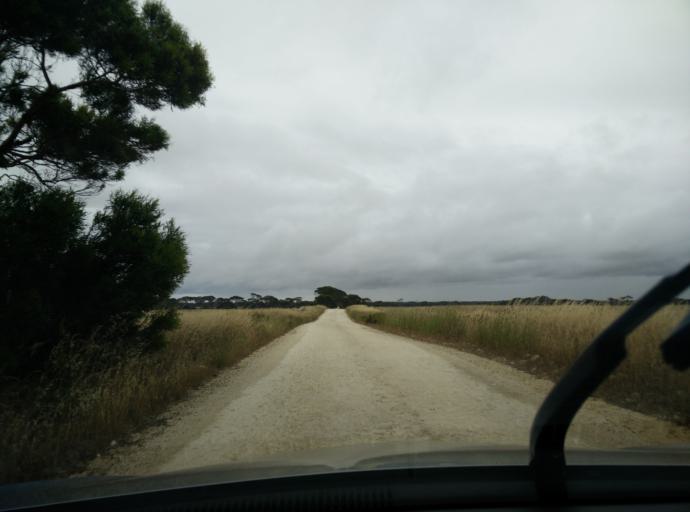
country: AU
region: South Australia
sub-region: Kangaroo Island
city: Kingscote
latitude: -35.8686
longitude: 137.5335
